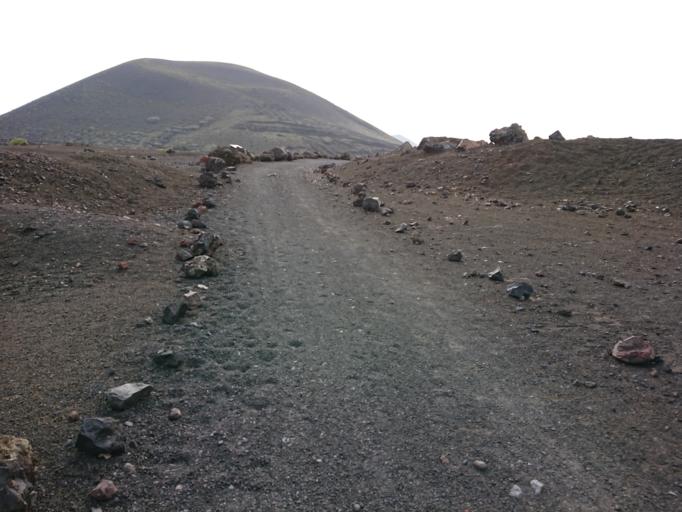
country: ES
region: Canary Islands
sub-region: Provincia de Las Palmas
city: Tias
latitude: 29.0039
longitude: -13.6766
